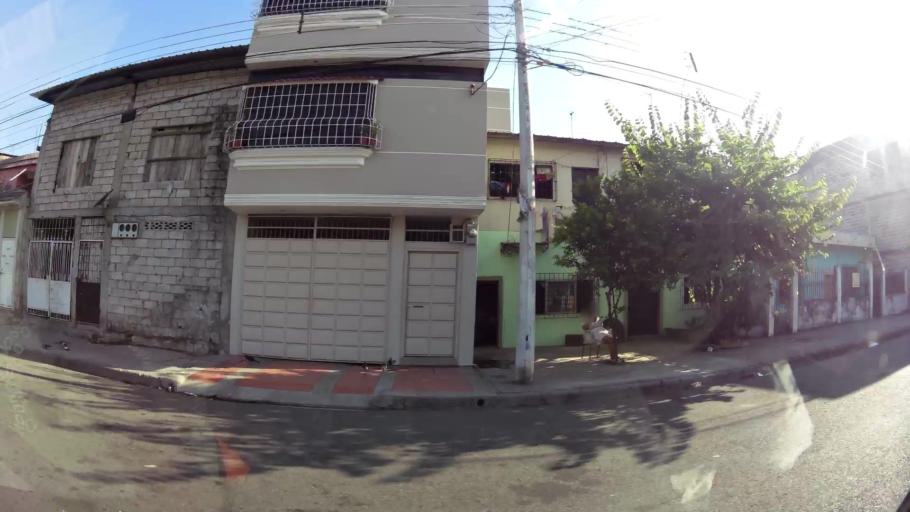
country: EC
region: Guayas
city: Guayaquil
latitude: -2.2178
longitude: -79.9206
